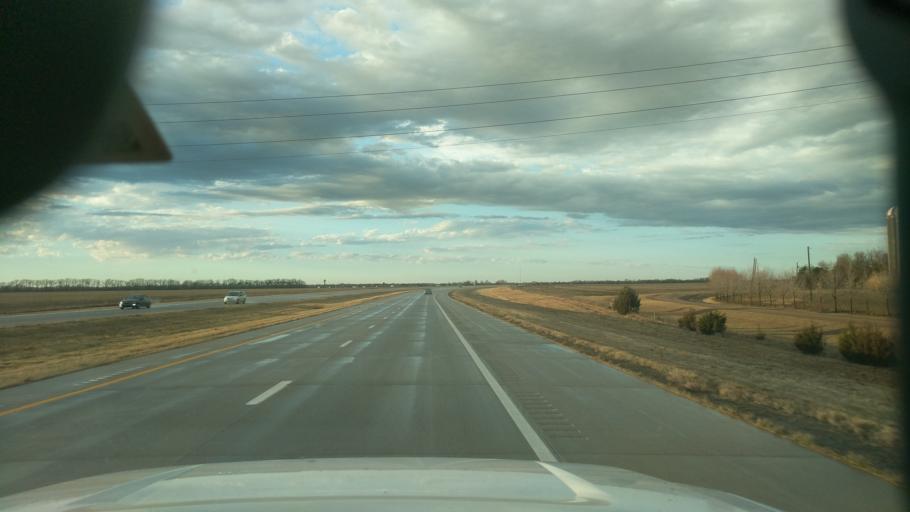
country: US
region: Kansas
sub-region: Harvey County
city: Hesston
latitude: 38.1169
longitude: -97.3895
